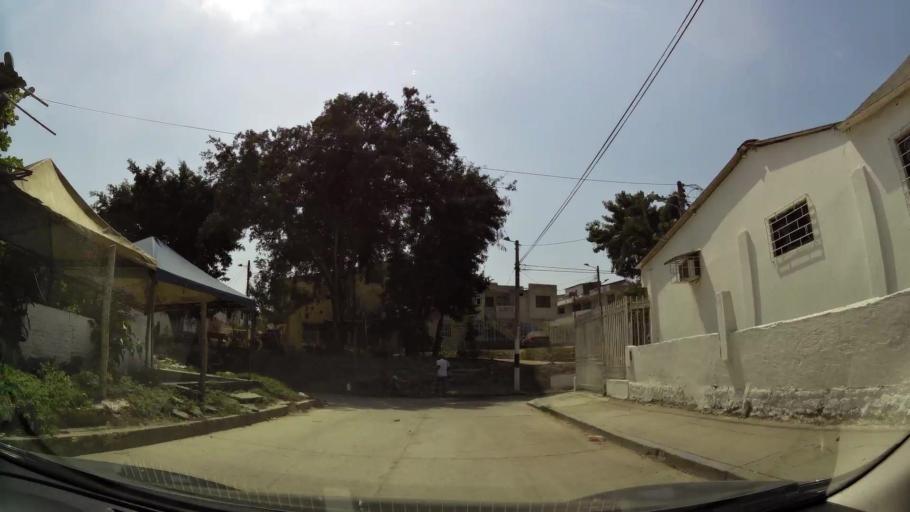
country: CO
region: Bolivar
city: Cartagena
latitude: 10.4017
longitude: -75.4904
